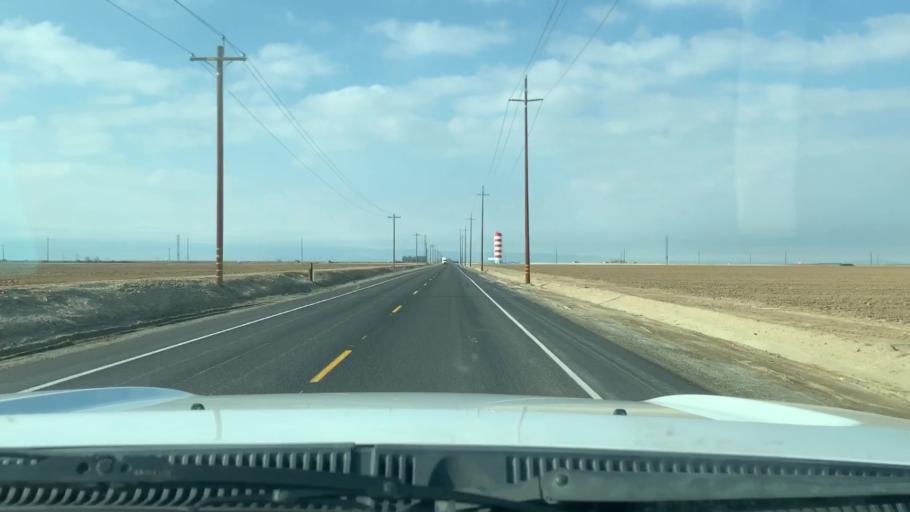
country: US
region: California
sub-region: Kern County
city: Buttonwillow
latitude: 35.4424
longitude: -119.4414
